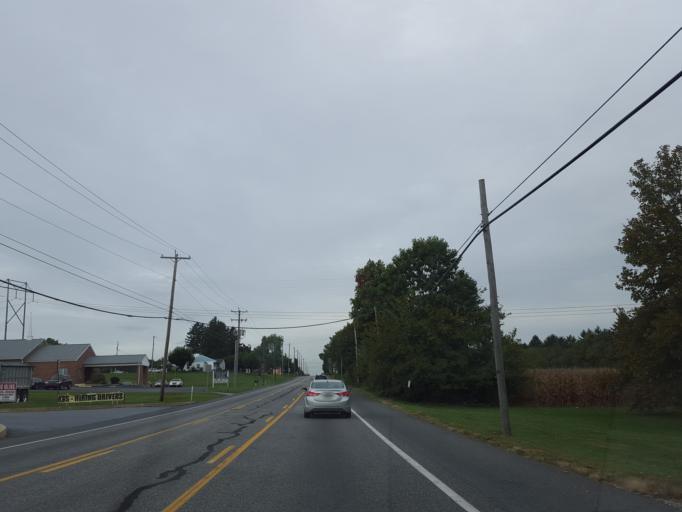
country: US
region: Pennsylvania
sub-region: York County
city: Weigelstown
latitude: 39.9287
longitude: -76.8396
